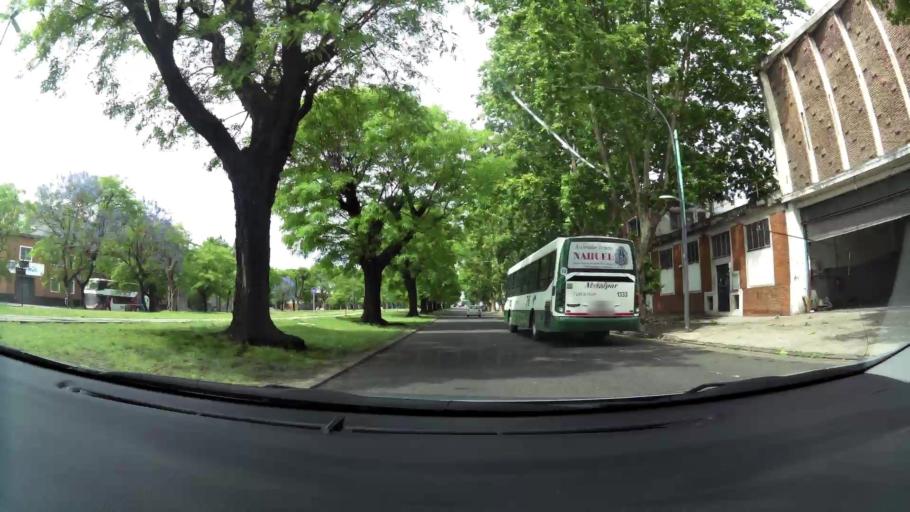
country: AR
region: Buenos Aires
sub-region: Partido de Lanus
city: Lanus
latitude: -34.6572
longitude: -58.4228
